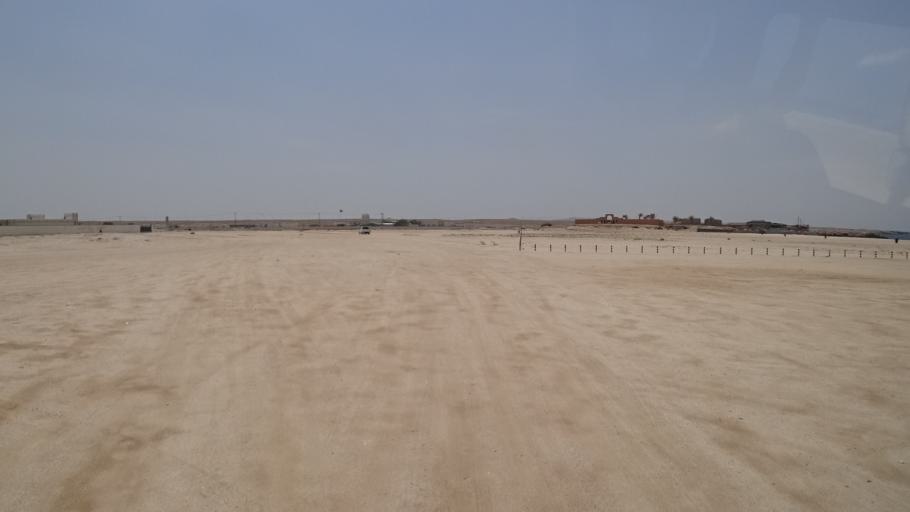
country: OM
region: Ash Sharqiyah
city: Sur
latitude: 22.5322
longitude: 59.7657
